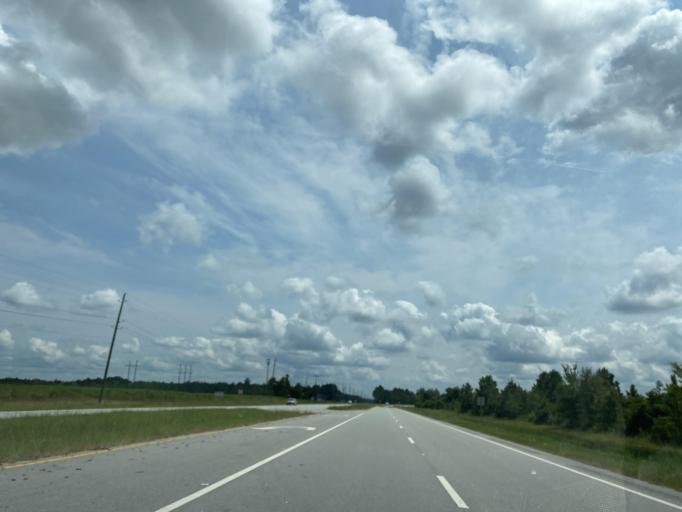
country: US
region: Georgia
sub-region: Ware County
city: Deenwood
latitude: 31.2519
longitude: -82.4293
